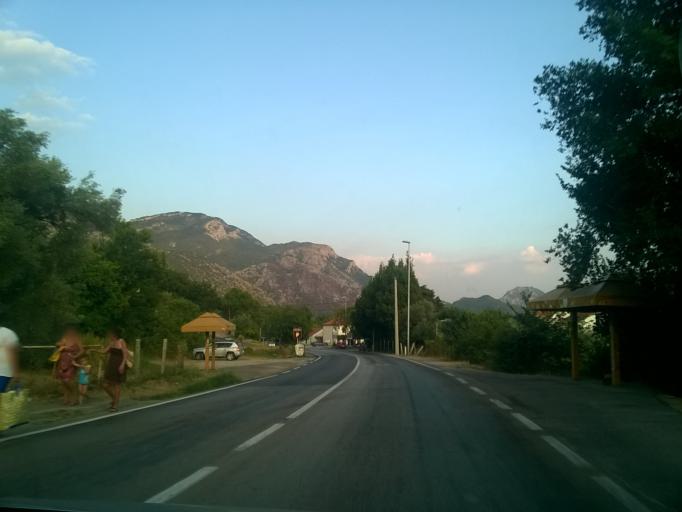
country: ME
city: Petrovac na Moru
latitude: 42.2002
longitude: 18.9642
